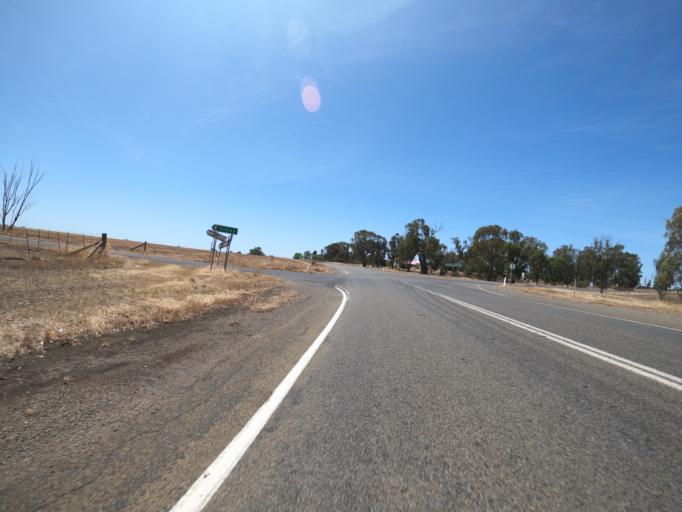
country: AU
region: Victoria
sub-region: Moira
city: Yarrawonga
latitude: -36.0993
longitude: 145.9949
